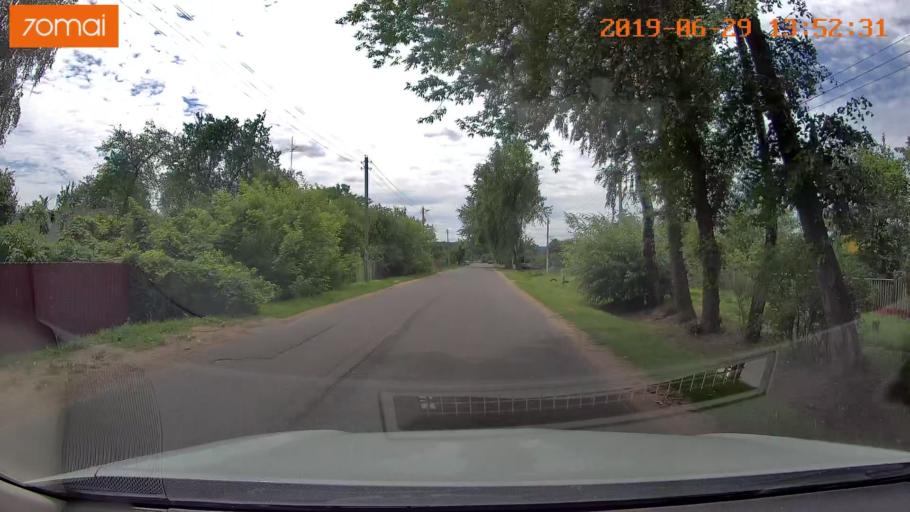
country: BY
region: Minsk
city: Slutsk
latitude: 52.9949
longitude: 27.5541
